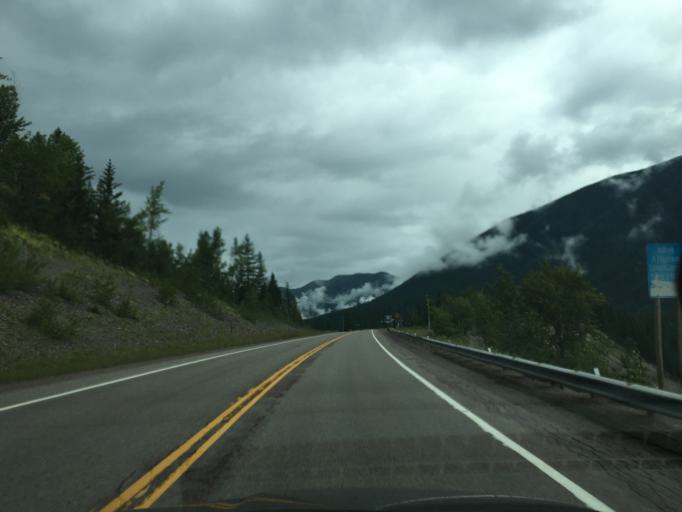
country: US
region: Montana
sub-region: Flathead County
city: Bigfork
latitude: 48.2803
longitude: -113.6073
